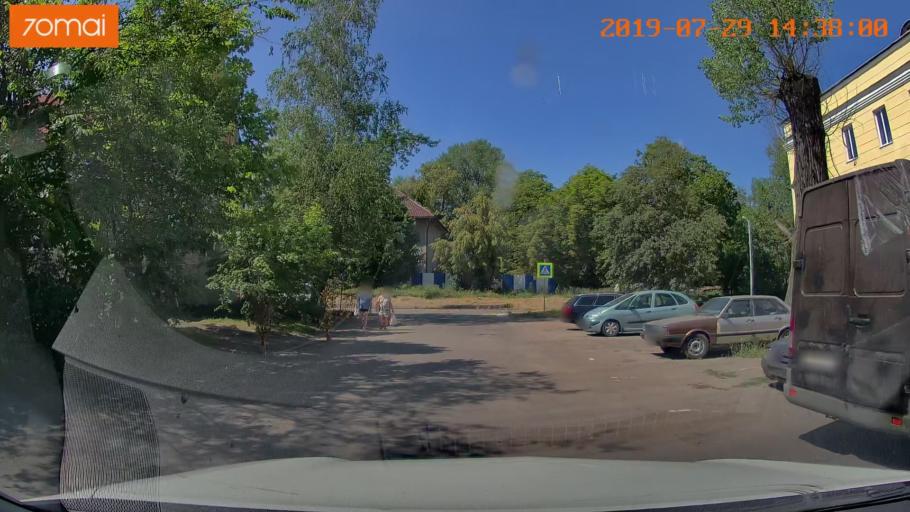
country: RU
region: Kaliningrad
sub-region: Gorod Kaliningrad
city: Baltiysk
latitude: 54.6489
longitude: 19.9014
